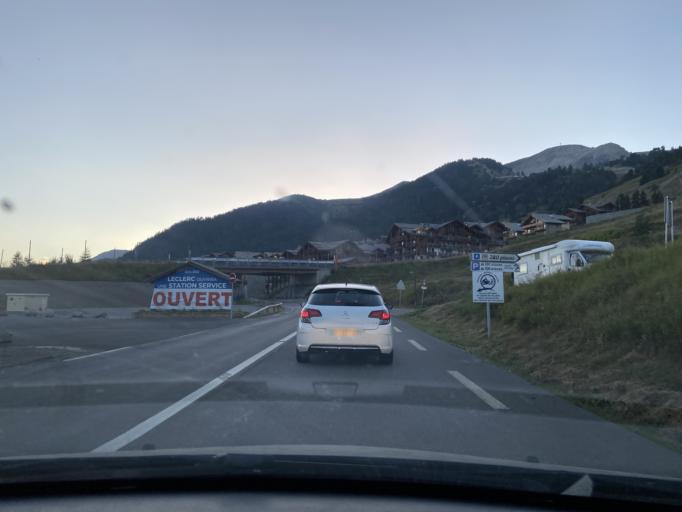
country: IT
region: Piedmont
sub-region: Provincia di Torino
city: Claviere
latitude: 44.9341
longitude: 6.7328
